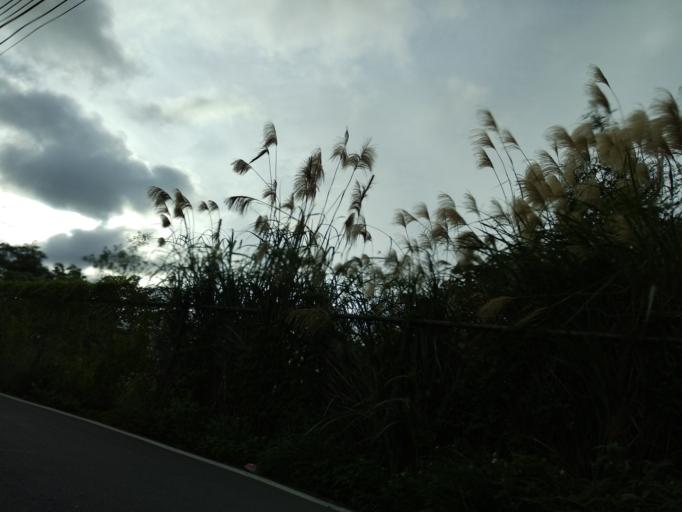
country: TW
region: Taiwan
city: Daxi
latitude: 24.9229
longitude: 121.1922
